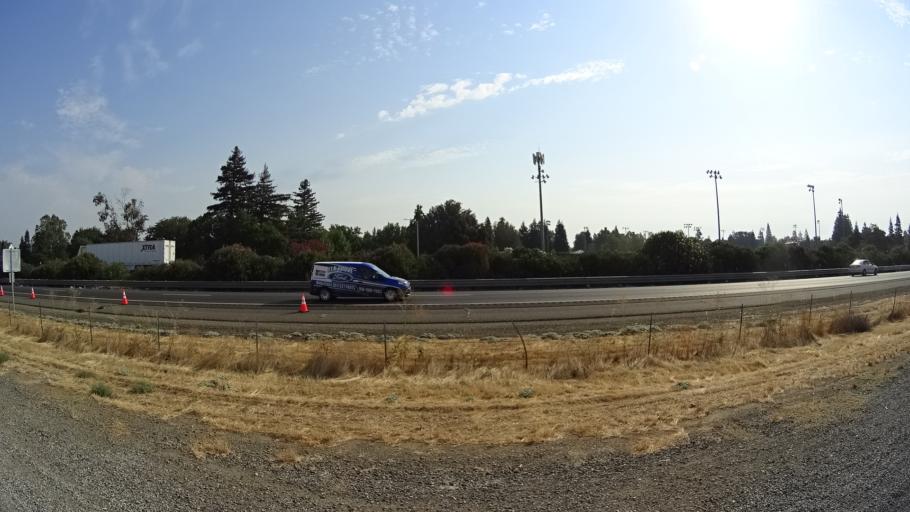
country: US
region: California
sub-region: Sacramento County
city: Elk Grove
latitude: 38.3895
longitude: -121.3754
